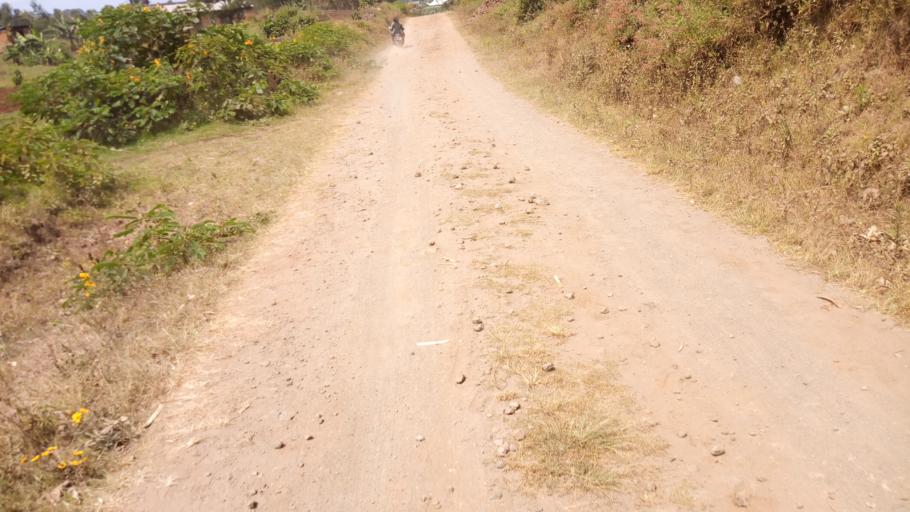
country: UG
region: Western Region
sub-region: Kisoro District
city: Kisoro
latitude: -1.3148
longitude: 29.7167
